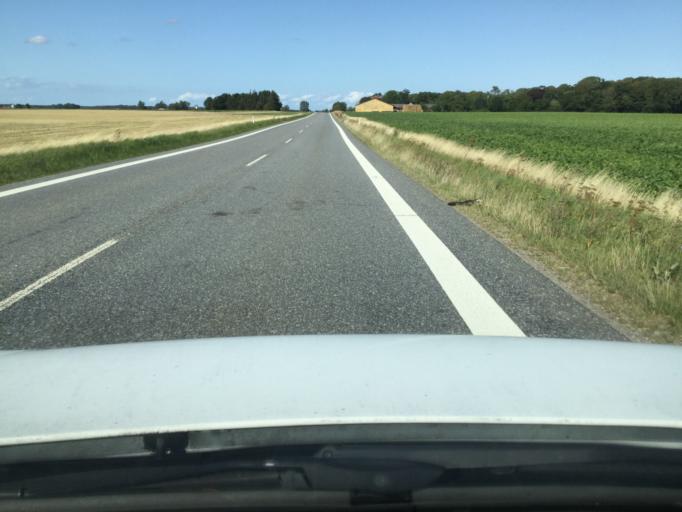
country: DK
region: Zealand
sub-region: Lolland Kommune
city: Rodby
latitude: 54.7257
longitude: 11.3870
